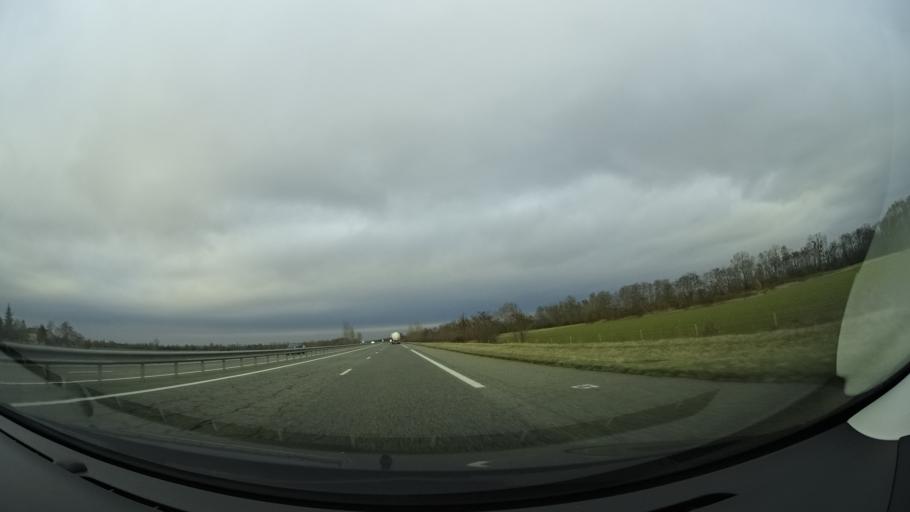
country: FR
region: Midi-Pyrenees
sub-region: Departement de l'Ariege
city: Pamiers
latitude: 43.1717
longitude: 1.6213
